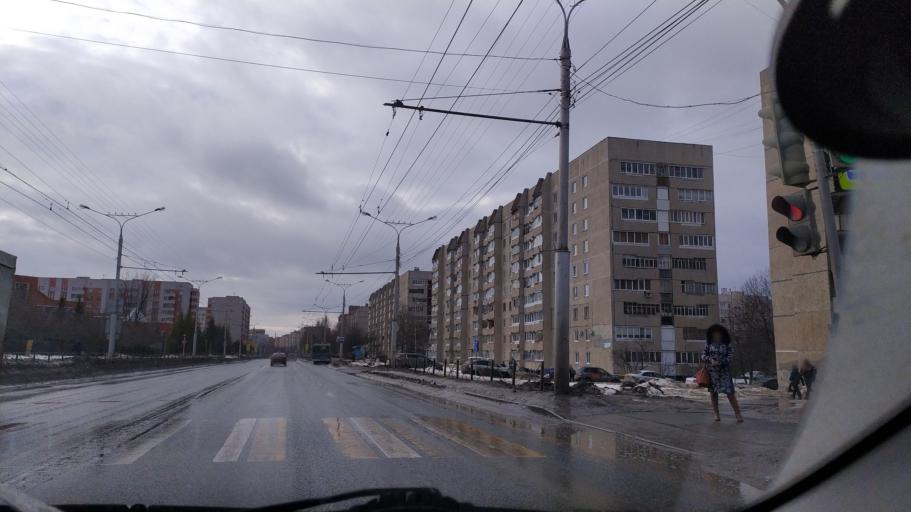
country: RU
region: Chuvashia
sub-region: Cheboksarskiy Rayon
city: Cheboksary
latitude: 56.1388
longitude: 47.1706
